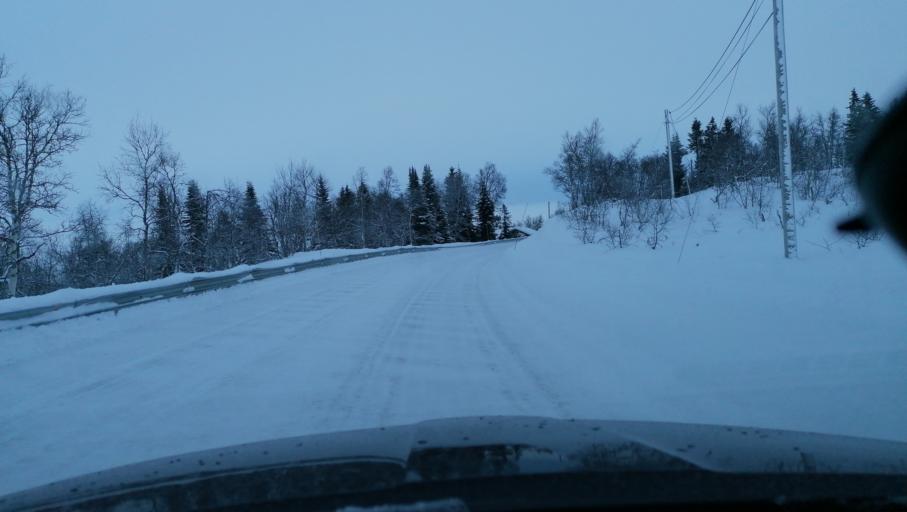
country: NO
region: Aust-Agder
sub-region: Bykle
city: Hovden
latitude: 59.6391
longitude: 7.4536
